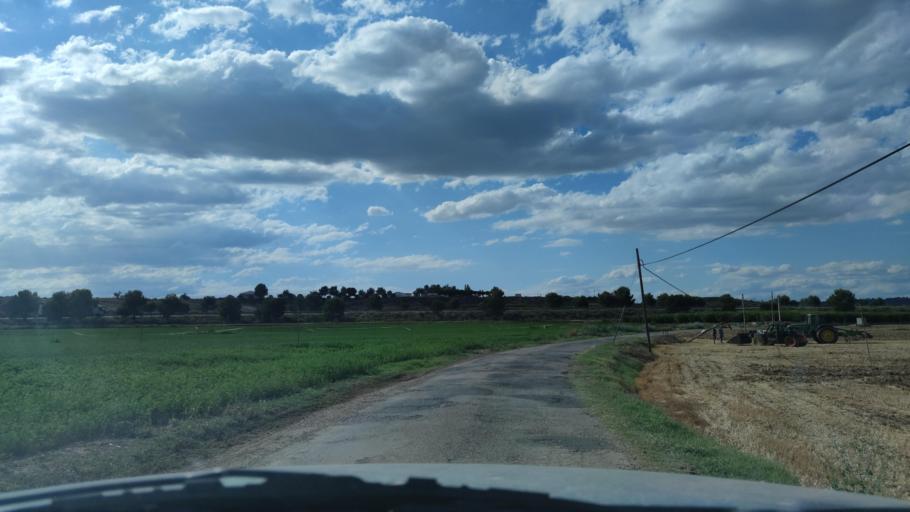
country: ES
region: Catalonia
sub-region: Provincia de Lleida
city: Alcarras
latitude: 41.5993
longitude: 0.5289
